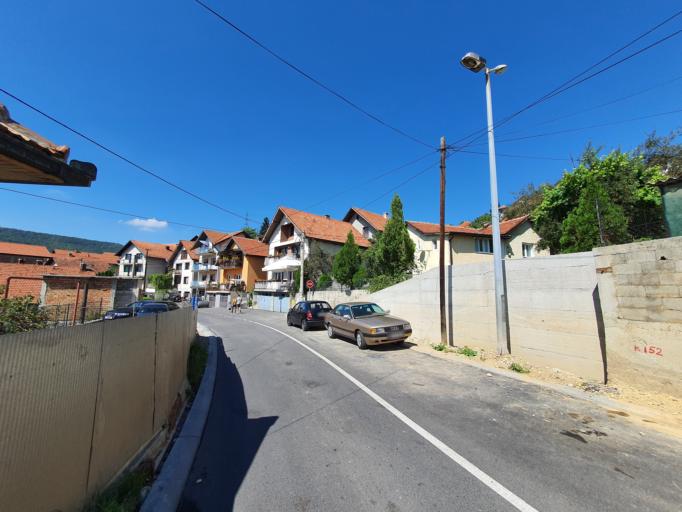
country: RS
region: Central Serbia
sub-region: Zlatiborski Okrug
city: Uzice
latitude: 43.8565
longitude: 19.8532
